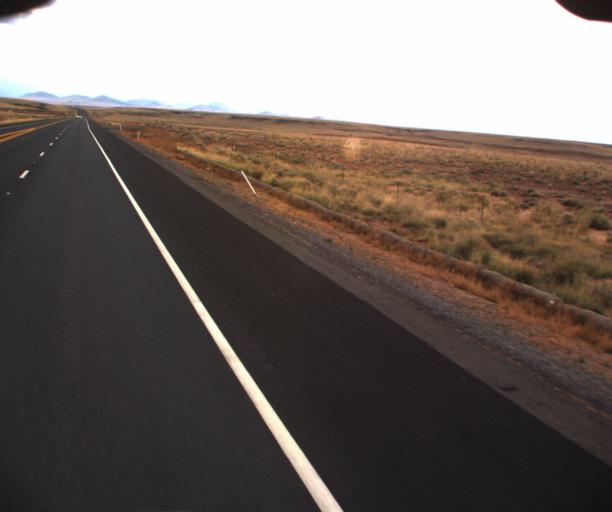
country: US
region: Arizona
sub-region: Coconino County
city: Tuba City
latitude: 35.7147
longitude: -111.4892
